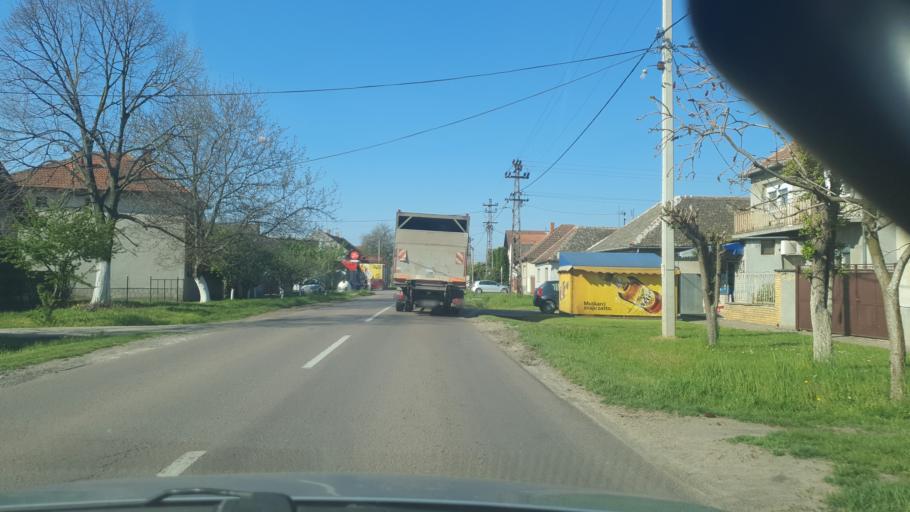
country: RS
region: Autonomna Pokrajina Vojvodina
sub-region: Zapadnobacki Okrug
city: Sombor
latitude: 45.7704
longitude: 19.2692
